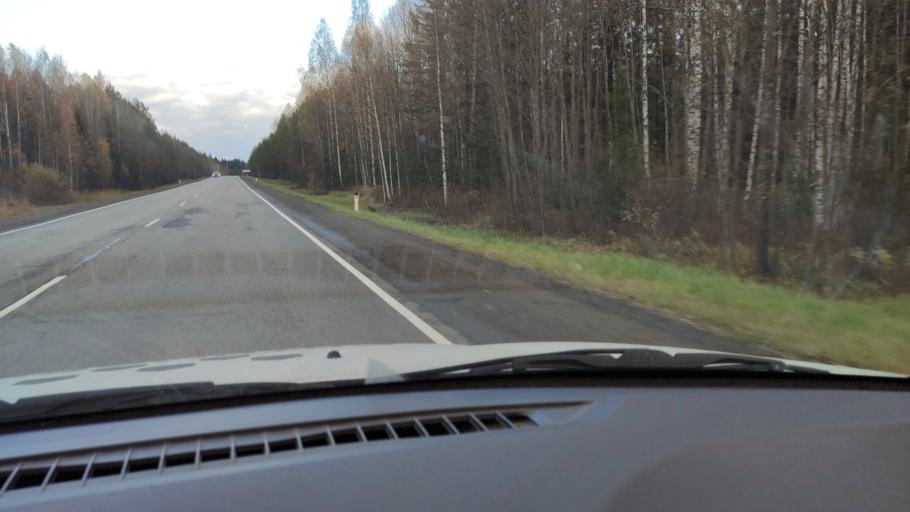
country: RU
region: Kirov
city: Belaya Kholunitsa
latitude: 58.9011
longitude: 50.9325
